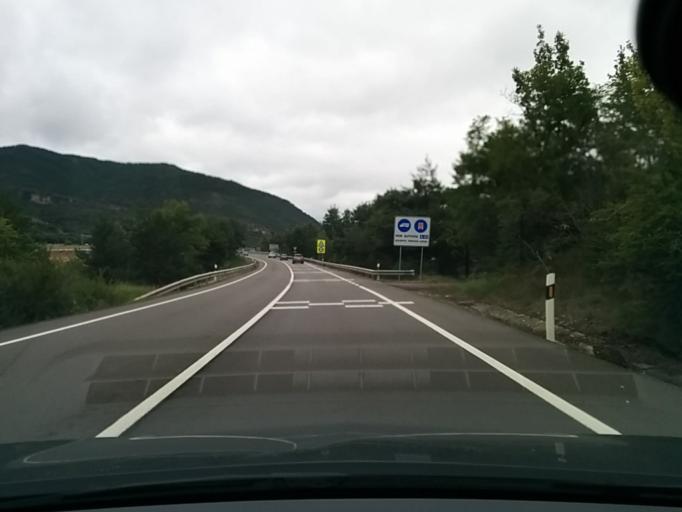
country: ES
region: Aragon
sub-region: Provincia de Huesca
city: Sabinanigo
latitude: 42.4807
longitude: -0.3751
